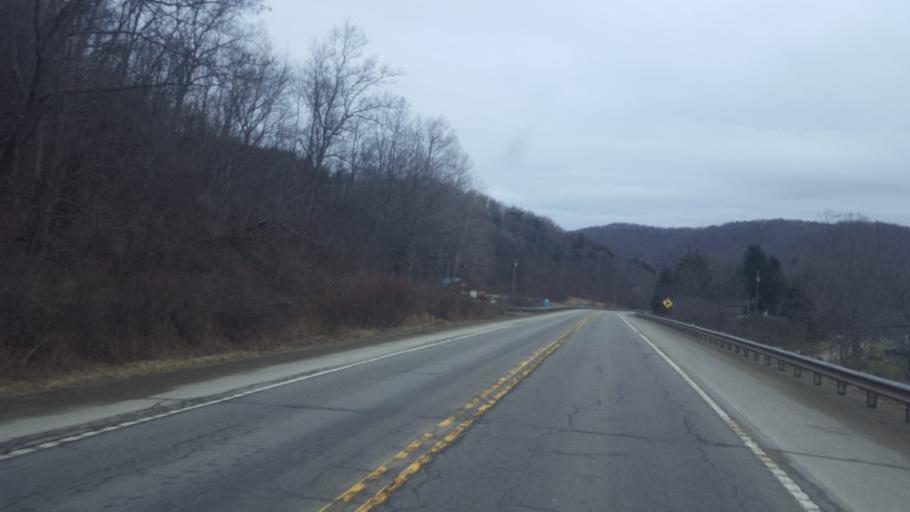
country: US
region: Pennsylvania
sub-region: Potter County
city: Coudersport
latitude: 41.7778
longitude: -78.1384
